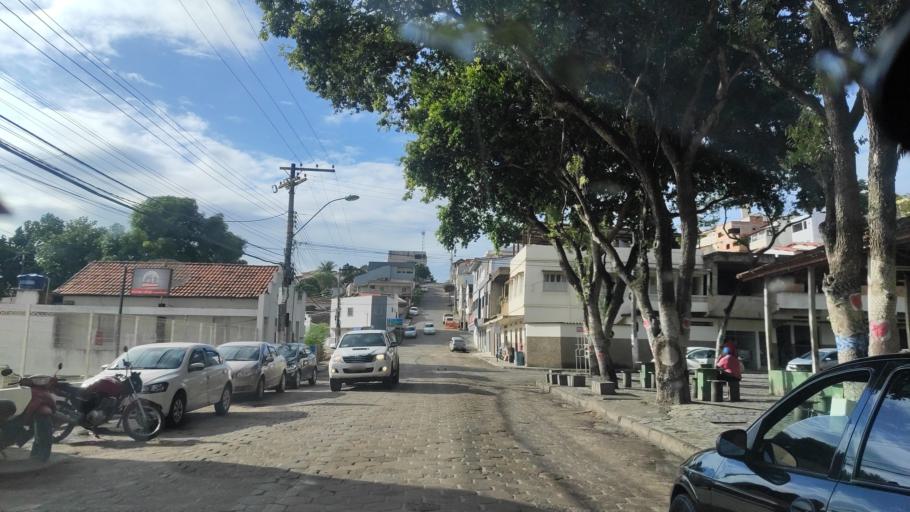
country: BR
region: Espirito Santo
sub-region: Nova Venecia
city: Nova Venecia
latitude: -18.7133
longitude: -40.3946
